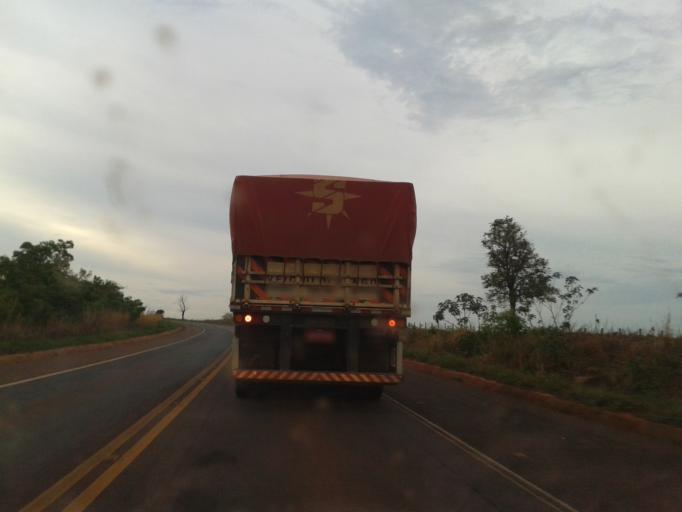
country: BR
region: Goias
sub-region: Santa Helena De Goias
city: Santa Helena de Goias
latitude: -17.9476
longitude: -50.5131
